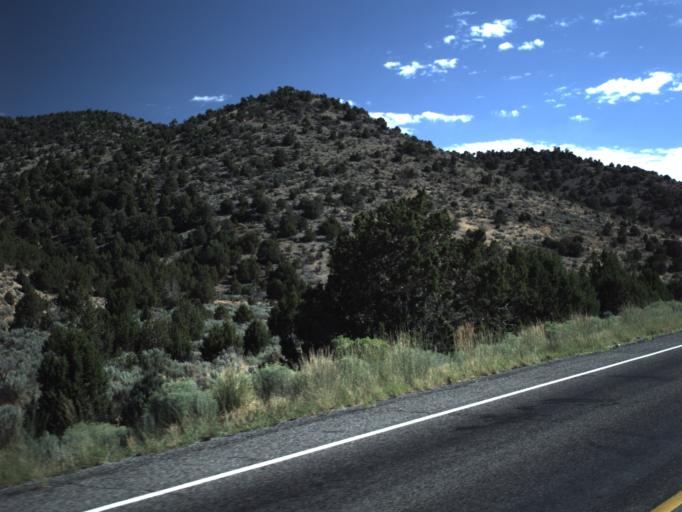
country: US
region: Utah
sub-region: Utah County
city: Genola
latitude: 39.9446
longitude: -112.1399
